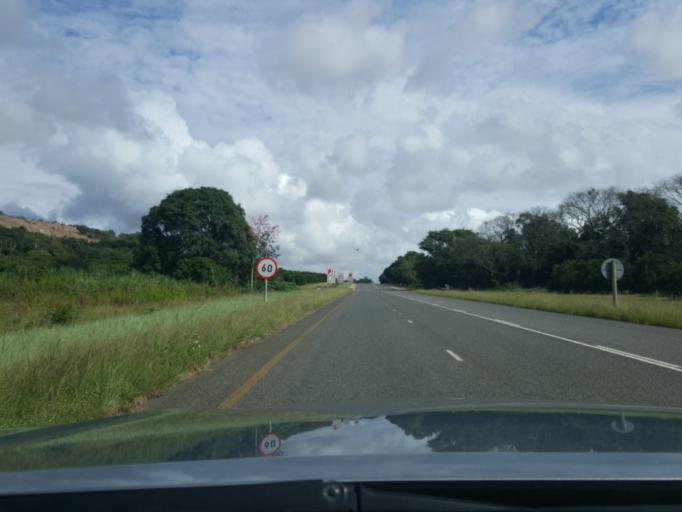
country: ZA
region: Mpumalanga
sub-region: Ehlanzeni District
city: Nelspruit
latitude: -25.4693
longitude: 31.0506
